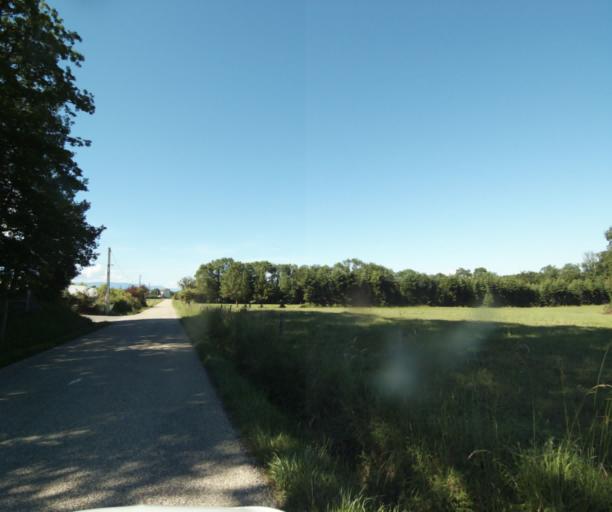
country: FR
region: Rhone-Alpes
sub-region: Departement de la Haute-Savoie
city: Sciez
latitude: 46.3098
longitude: 6.3822
